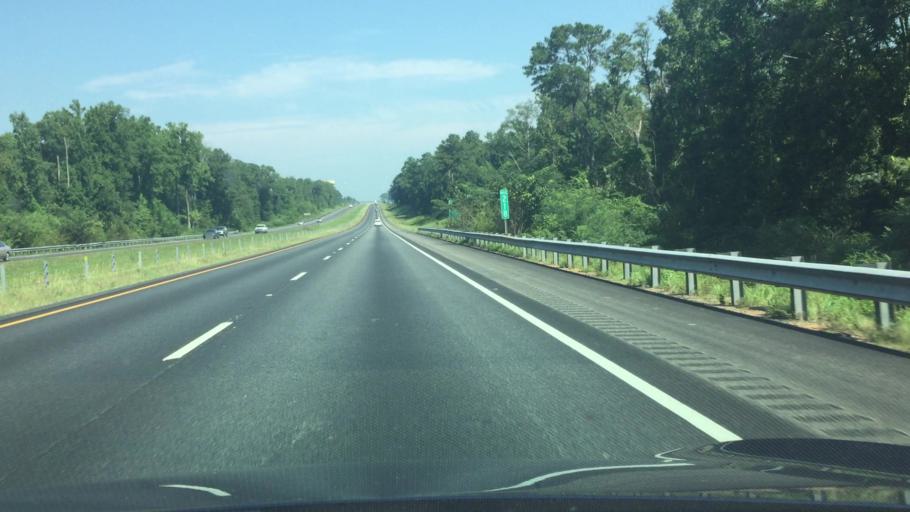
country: US
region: Alabama
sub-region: Chilton County
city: Thorsby
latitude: 32.9644
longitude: -86.6775
